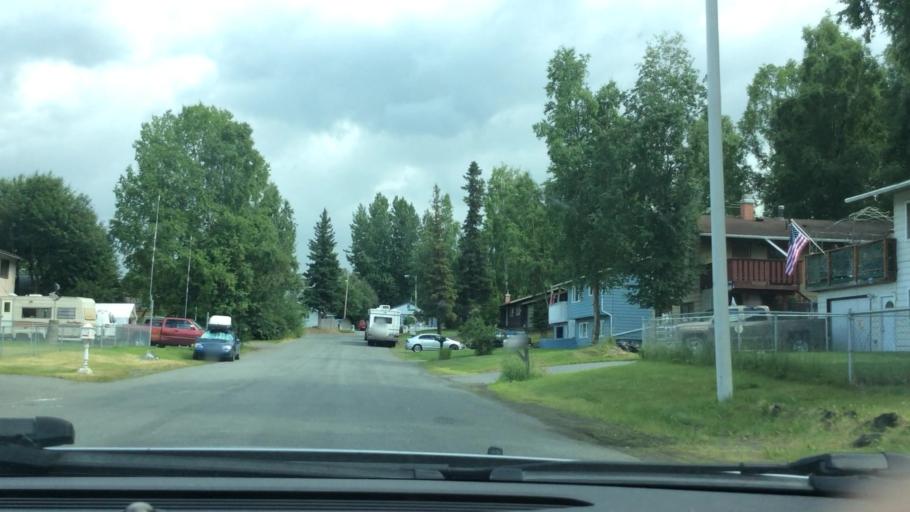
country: US
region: Alaska
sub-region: Anchorage Municipality
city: Elmendorf Air Force Base
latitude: 61.2214
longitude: -149.7507
